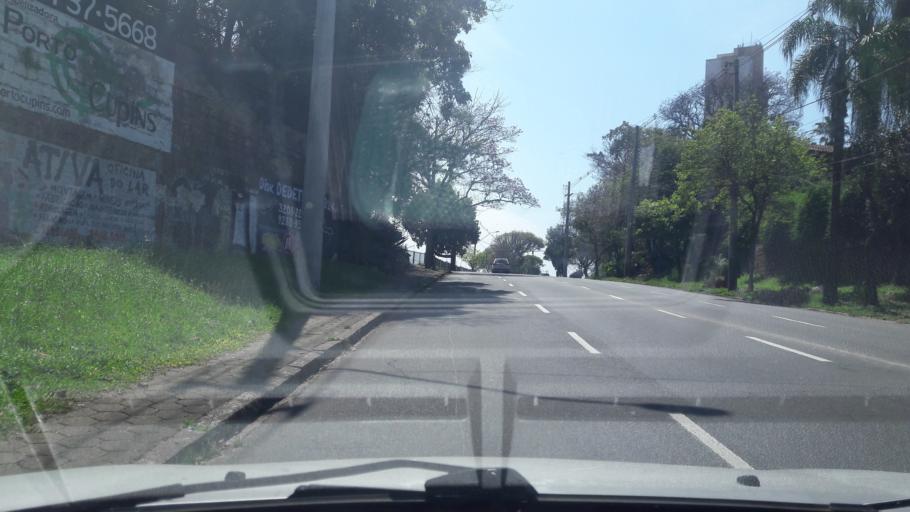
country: BR
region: Rio Grande do Sul
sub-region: Porto Alegre
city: Porto Alegre
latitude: -30.0789
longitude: -51.2441
